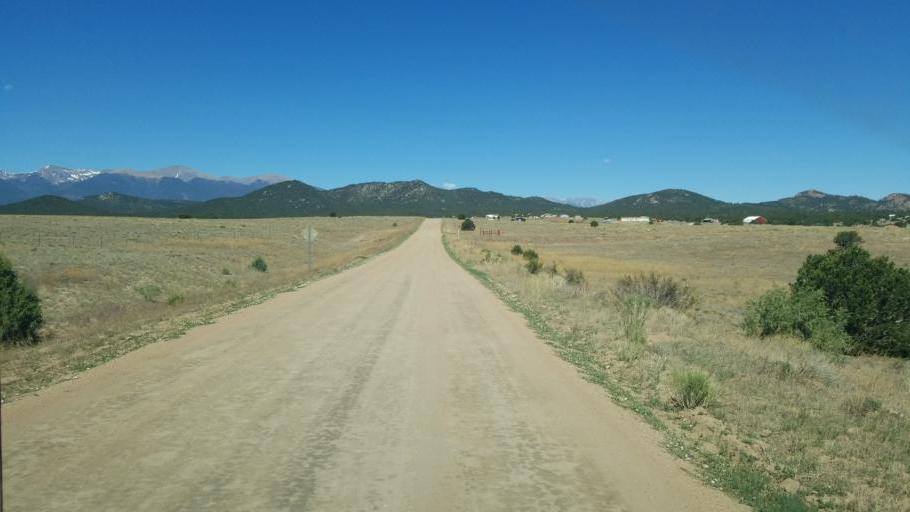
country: US
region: Colorado
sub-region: Custer County
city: Westcliffe
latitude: 38.2846
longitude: -105.5014
